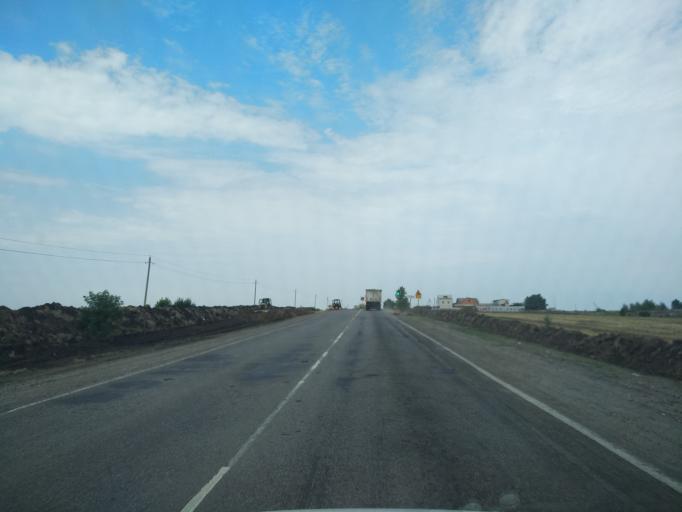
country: RU
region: Voronezj
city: Verkhnyaya Khava
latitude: 51.6763
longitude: 39.8100
